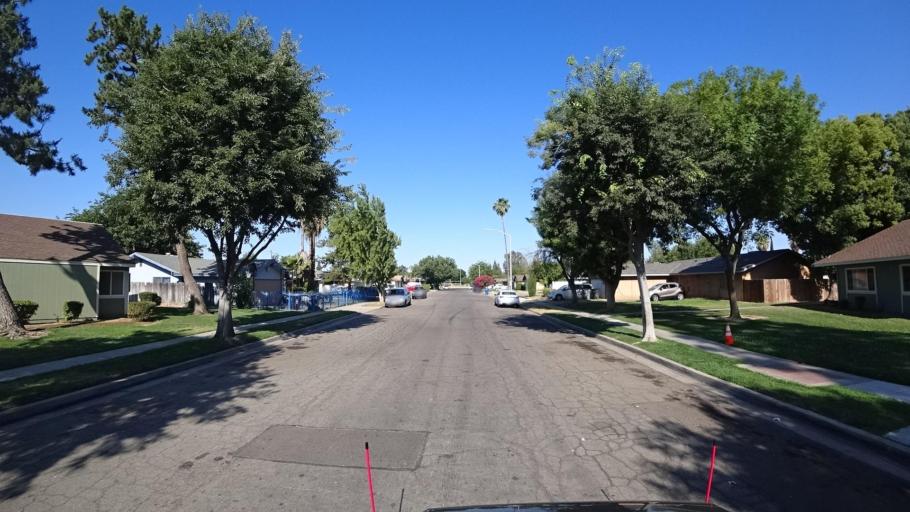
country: US
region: California
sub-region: Fresno County
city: West Park
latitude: 36.7276
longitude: -119.8203
